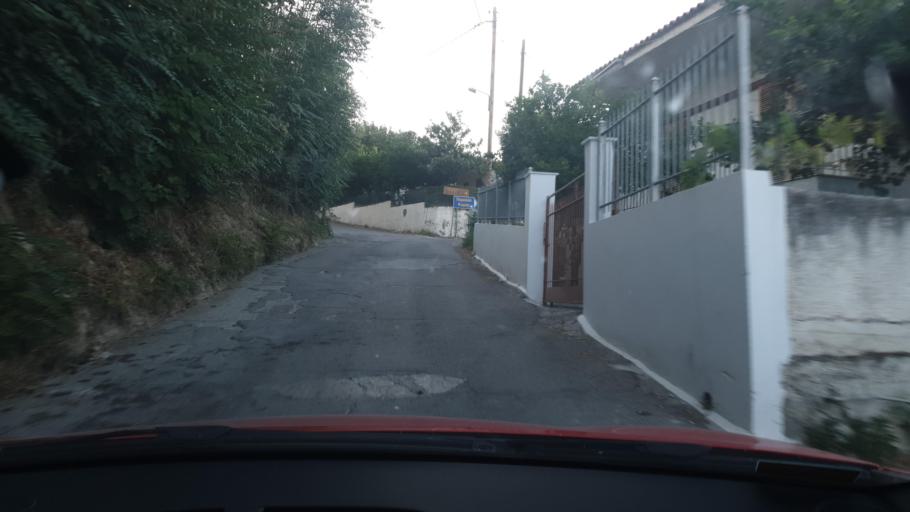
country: GR
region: Central Greece
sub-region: Nomos Evvoias
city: Oxilithos
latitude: 38.5773
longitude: 24.1138
